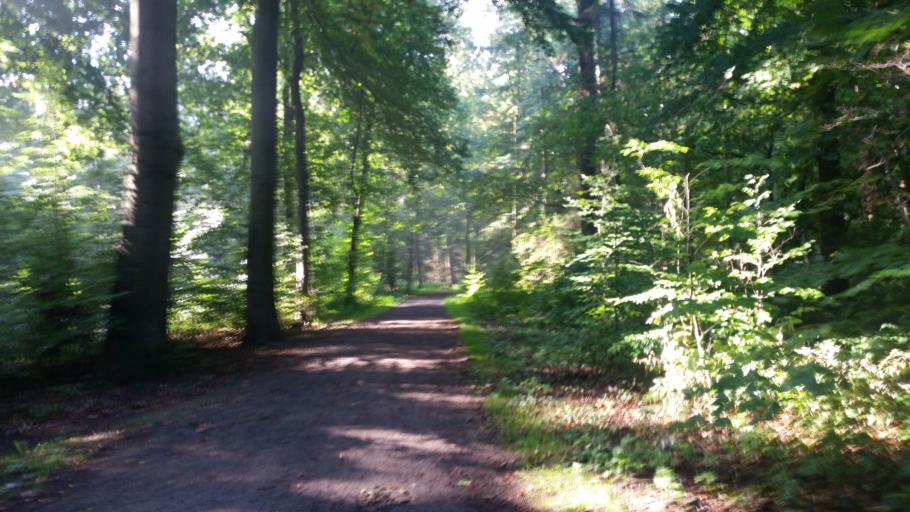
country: DE
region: Lower Saxony
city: Hannover
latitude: 52.3933
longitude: 9.7704
